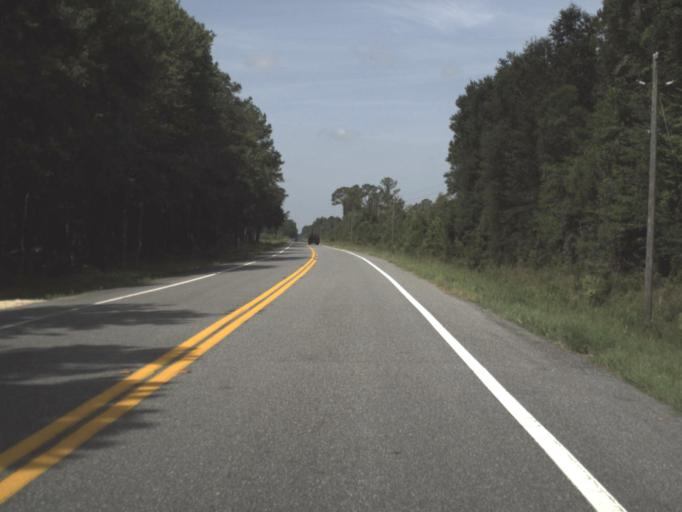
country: US
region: Florida
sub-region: Lafayette County
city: Mayo
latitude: 29.9490
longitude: -83.2597
